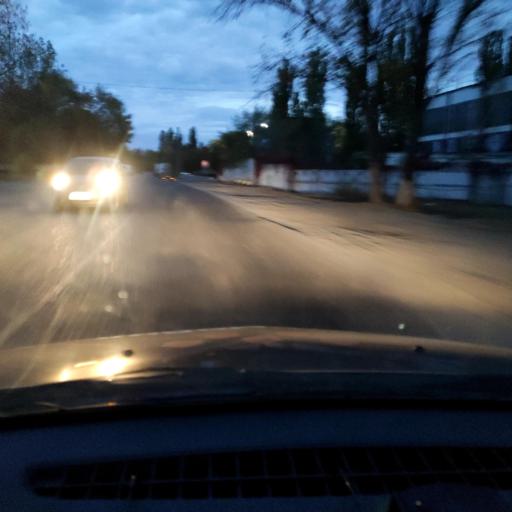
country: RU
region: Voronezj
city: Pridonskoy
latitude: 51.6770
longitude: 39.0919
